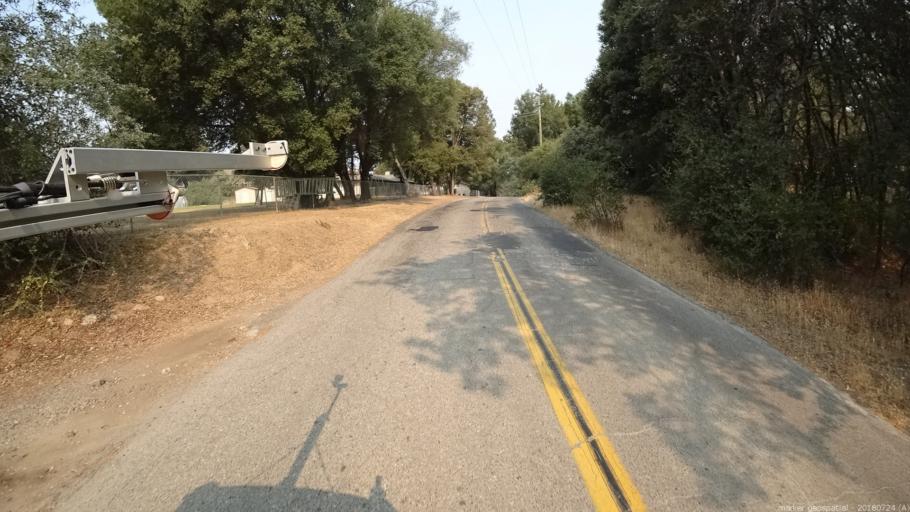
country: US
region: California
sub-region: Madera County
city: Oakhurst
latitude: 37.3078
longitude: -119.6197
